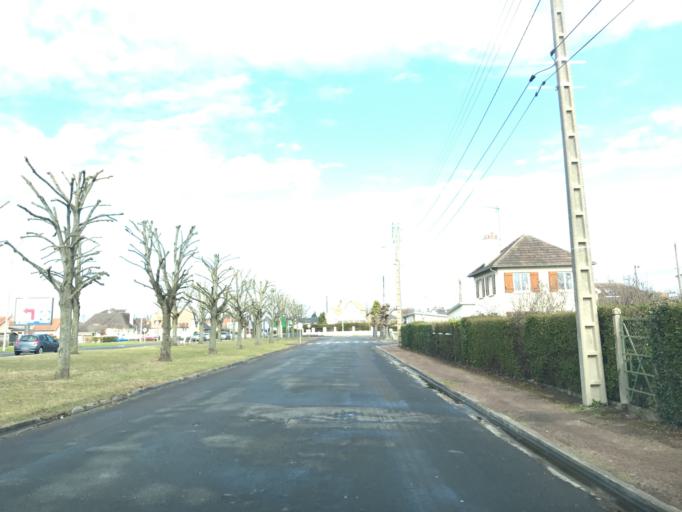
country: FR
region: Lower Normandy
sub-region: Departement du Calvados
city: Dives-sur-Mer
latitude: 49.2823
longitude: -0.1026
